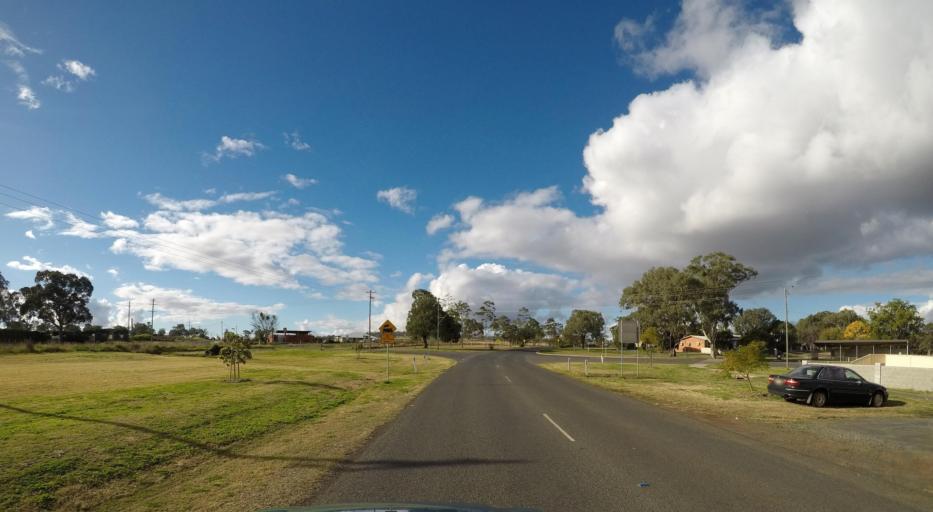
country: AU
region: Queensland
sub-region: Toowoomba
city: Westbrook
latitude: -27.7102
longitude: 151.6429
